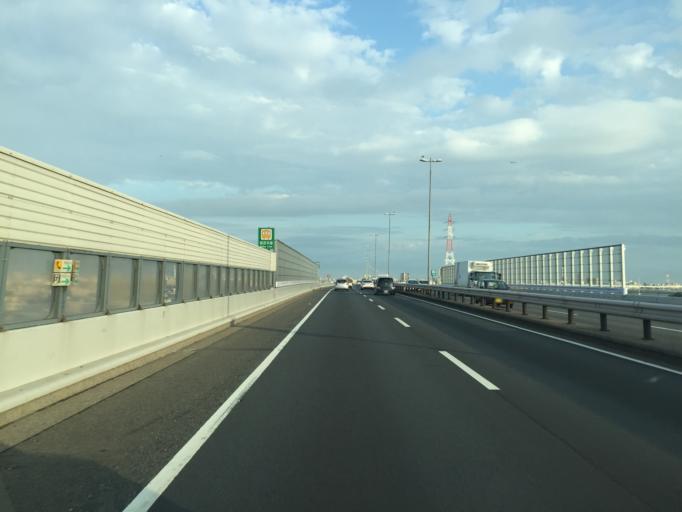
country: JP
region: Tokyo
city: Urayasu
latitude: 35.7136
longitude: 139.8516
